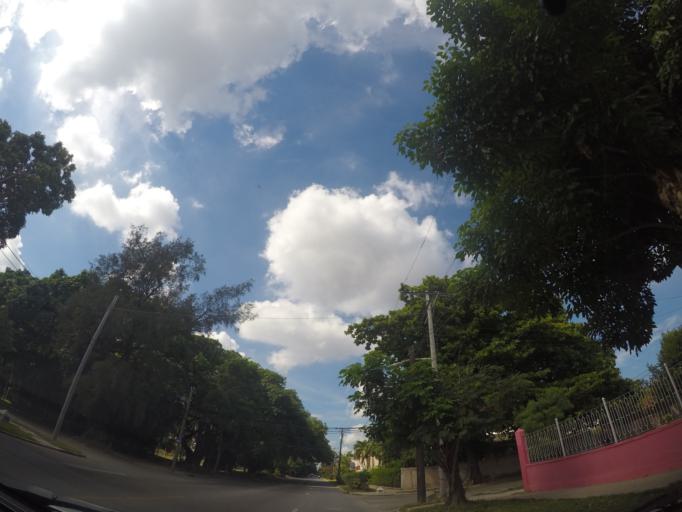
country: CU
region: La Habana
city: Havana
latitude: 23.1260
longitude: -82.4124
